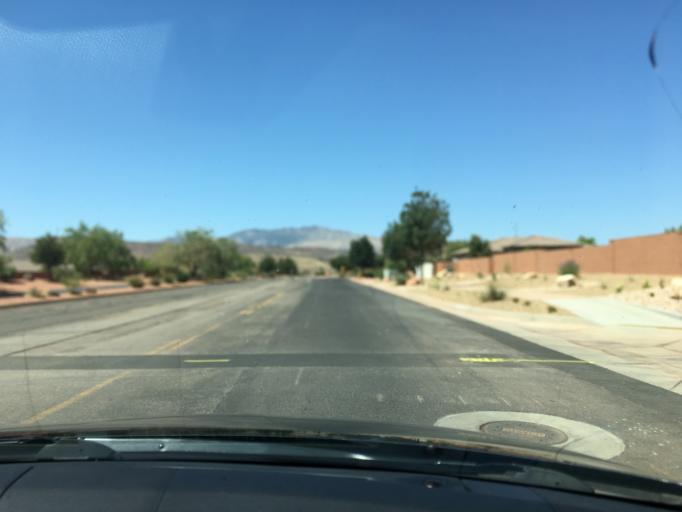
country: US
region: Utah
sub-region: Washington County
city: Ivins
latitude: 37.1683
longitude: -113.6858
